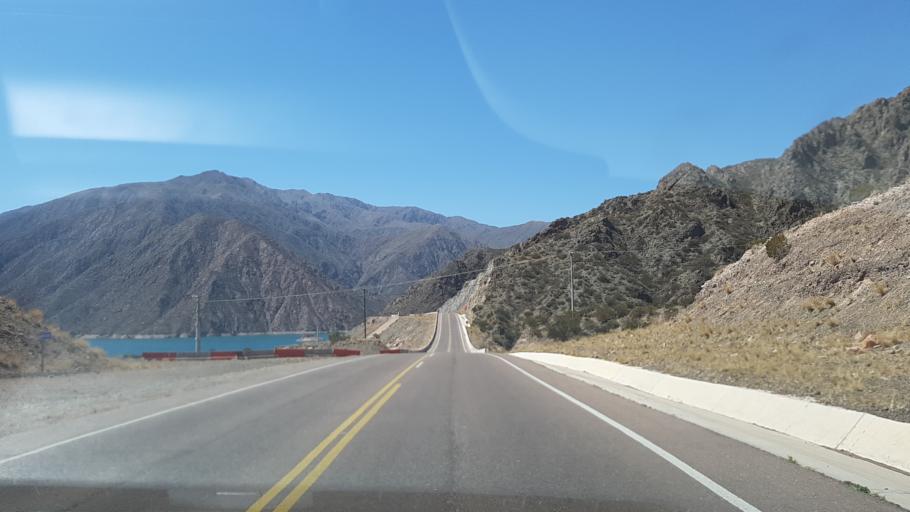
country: AR
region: Mendoza
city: Lujan de Cuyo
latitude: -32.9925
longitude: -69.1618
